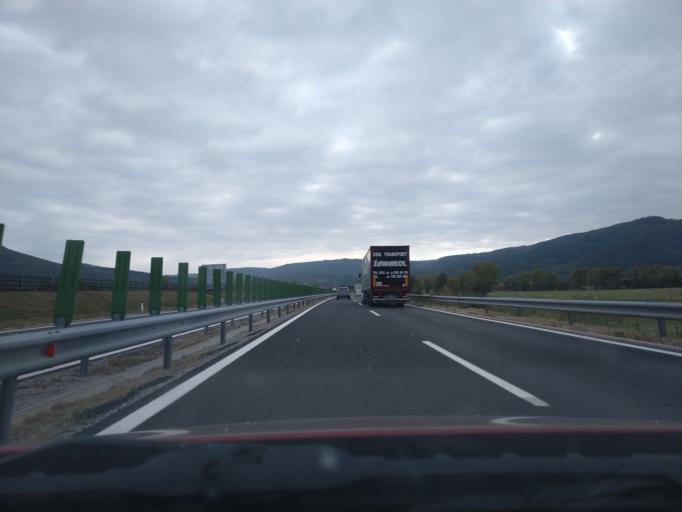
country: SI
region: Vipava
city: Vipava
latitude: 45.8236
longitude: 13.9606
